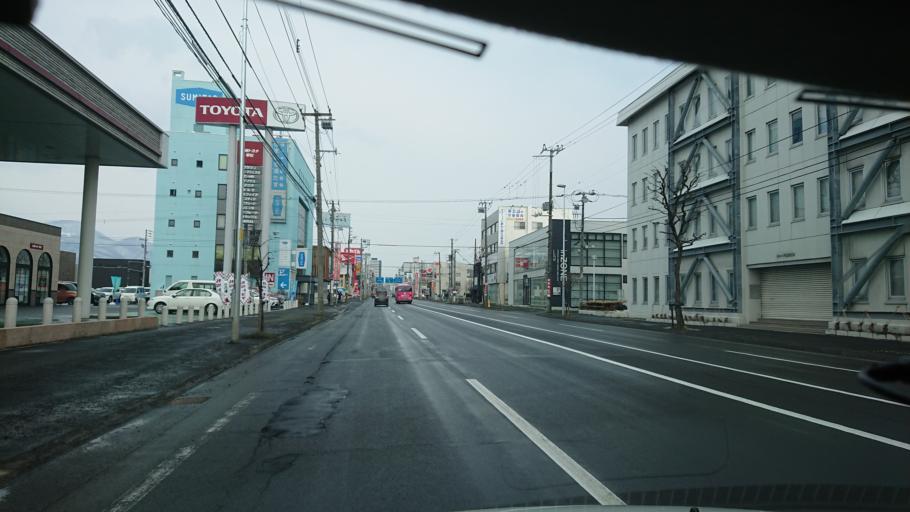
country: JP
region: Hokkaido
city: Sapporo
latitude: 43.0667
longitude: 141.3110
